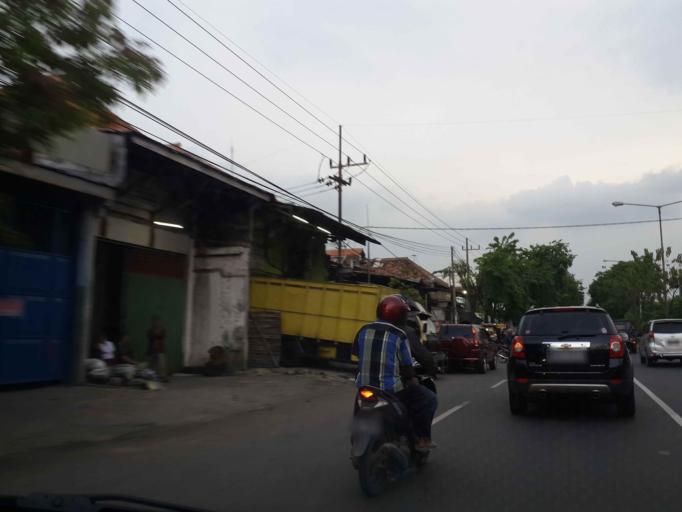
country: ID
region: East Java
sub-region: Kota Surabaya
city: Surabaya
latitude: -7.2510
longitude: 112.7207
